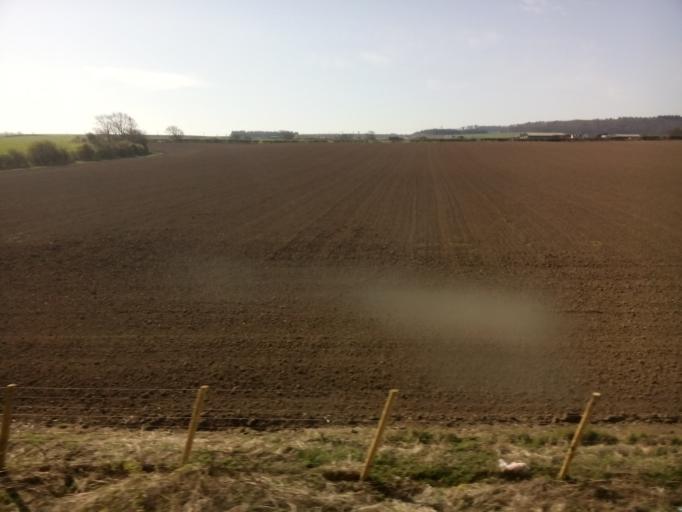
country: GB
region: Scotland
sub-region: East Lothian
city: Haddington
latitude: 56.0079
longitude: -2.7643
